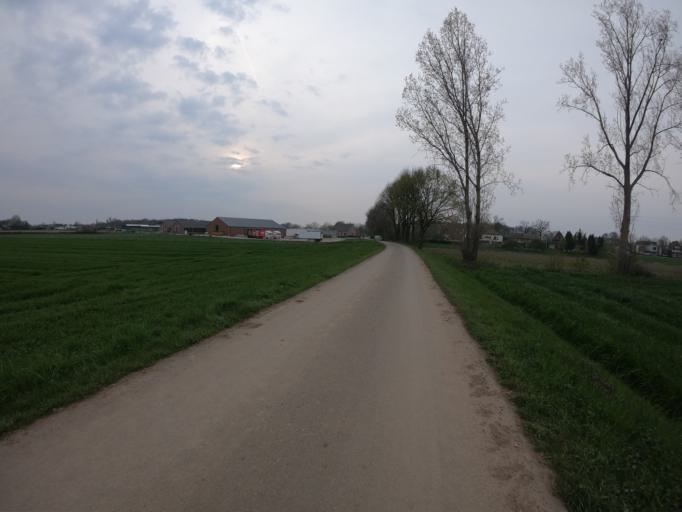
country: BE
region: Flanders
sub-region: Provincie Limburg
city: Maaseik
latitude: 51.0898
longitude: 5.7727
